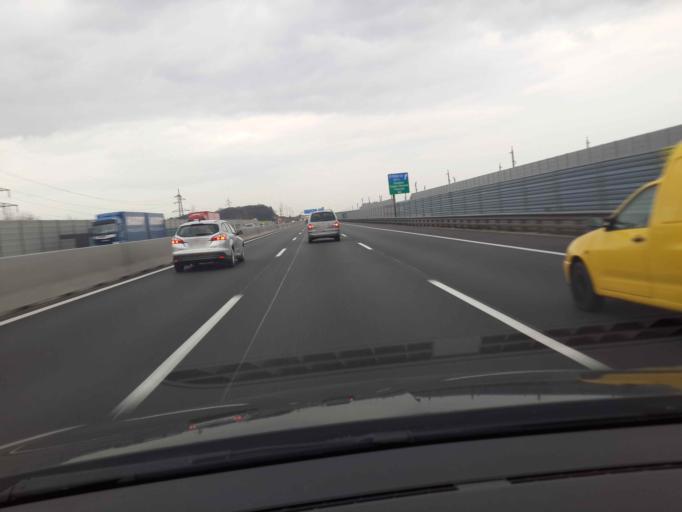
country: AT
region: Lower Austria
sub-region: Sankt Polten Stadt
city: Sankt Poelten
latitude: 48.1768
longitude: 15.6225
